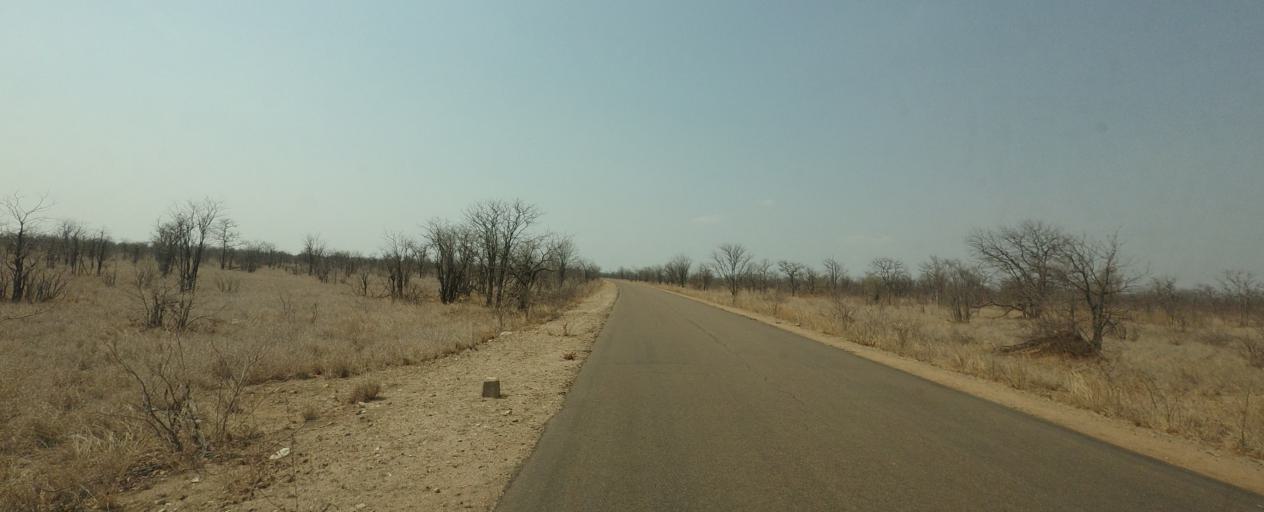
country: ZA
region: Limpopo
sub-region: Mopani District Municipality
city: Giyani
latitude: -23.3408
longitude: 31.3221
